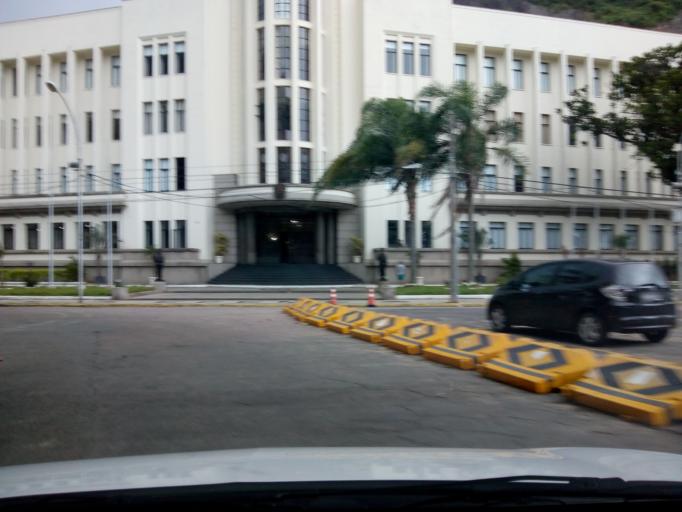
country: BR
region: Rio de Janeiro
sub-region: Rio De Janeiro
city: Rio de Janeiro
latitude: -22.9546
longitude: -43.1653
